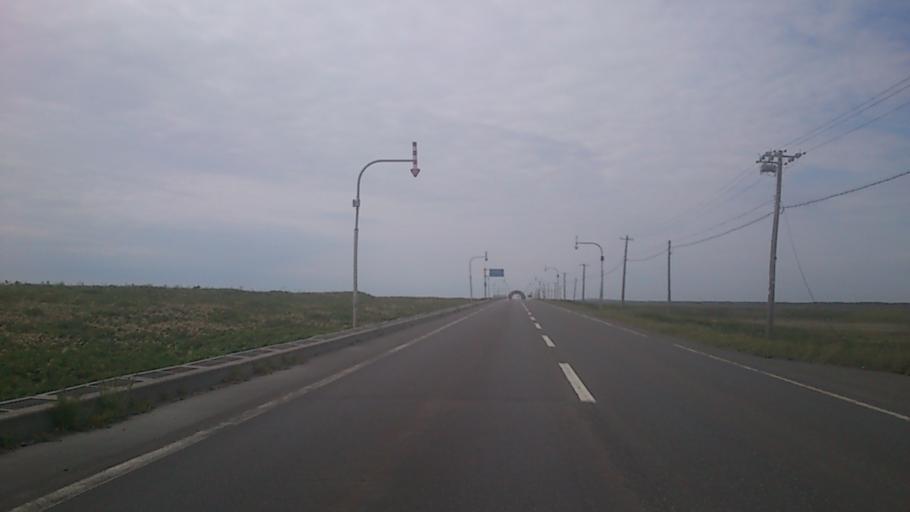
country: JP
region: Hokkaido
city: Makubetsu
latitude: 44.9982
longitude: 141.6836
